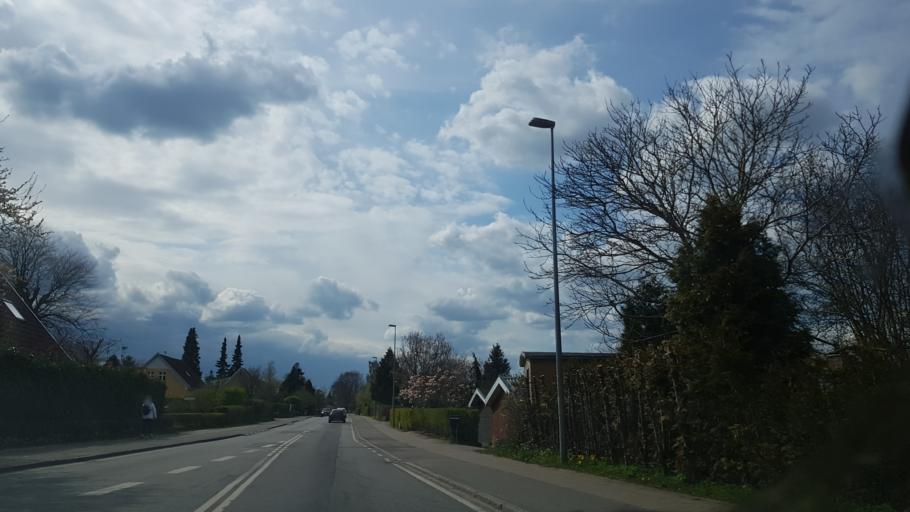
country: DK
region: Capital Region
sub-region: Allerod Kommune
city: Lillerod
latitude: 55.8685
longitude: 12.3468
